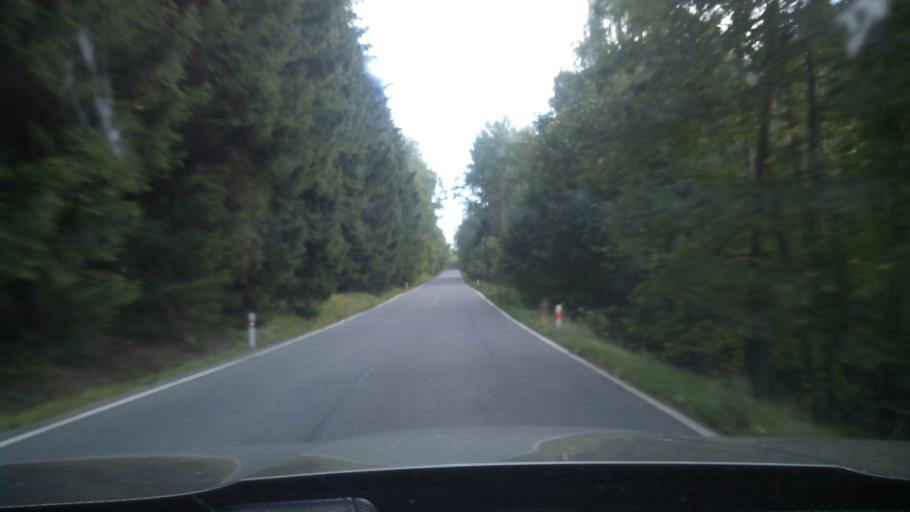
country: CZ
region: Plzensky
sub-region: Okres Klatovy
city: Kasperske Hory
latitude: 49.1405
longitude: 13.5758
